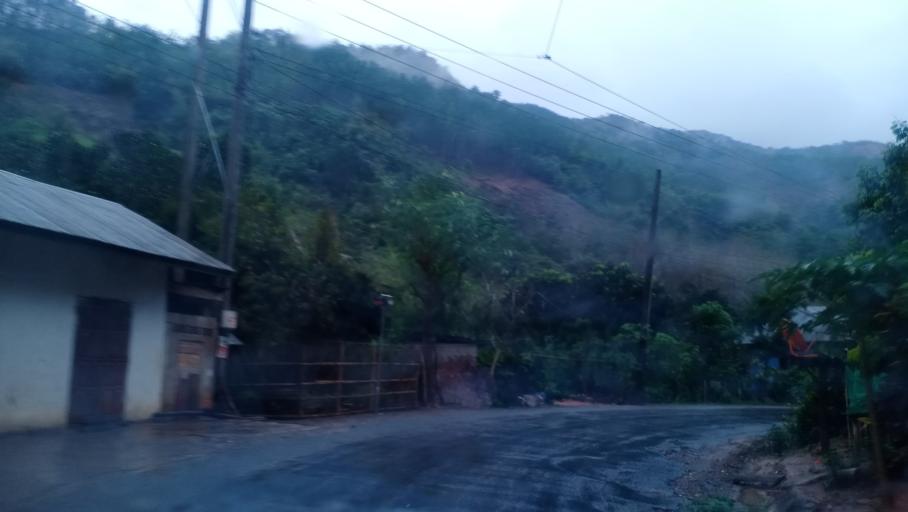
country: LA
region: Phongsali
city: Khoa
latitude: 21.0742
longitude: 102.5032
